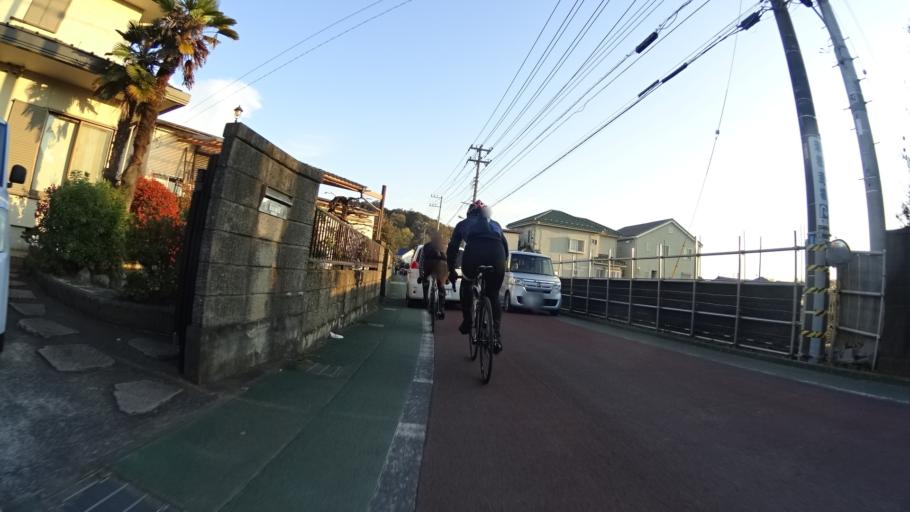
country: JP
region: Tokyo
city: Fussa
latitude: 35.7794
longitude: 139.3488
